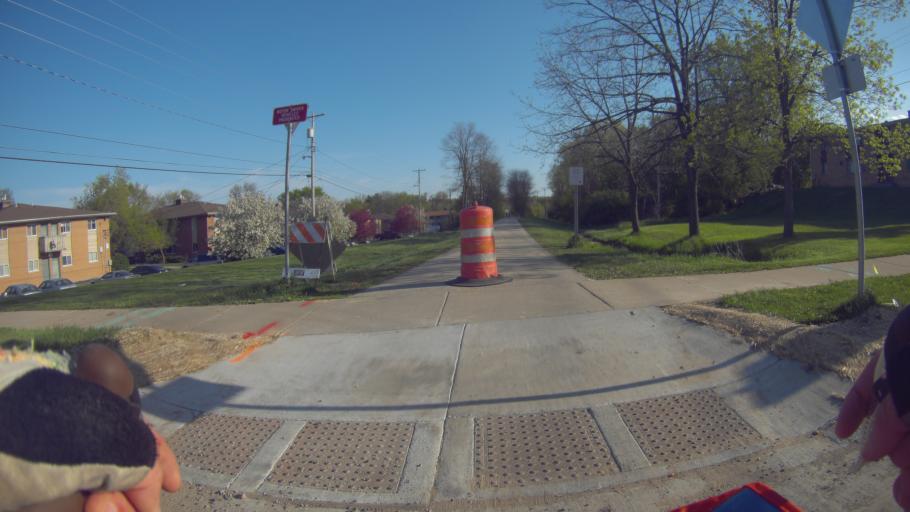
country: US
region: Wisconsin
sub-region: Dane County
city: Shorewood Hills
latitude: 43.0269
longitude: -89.4607
